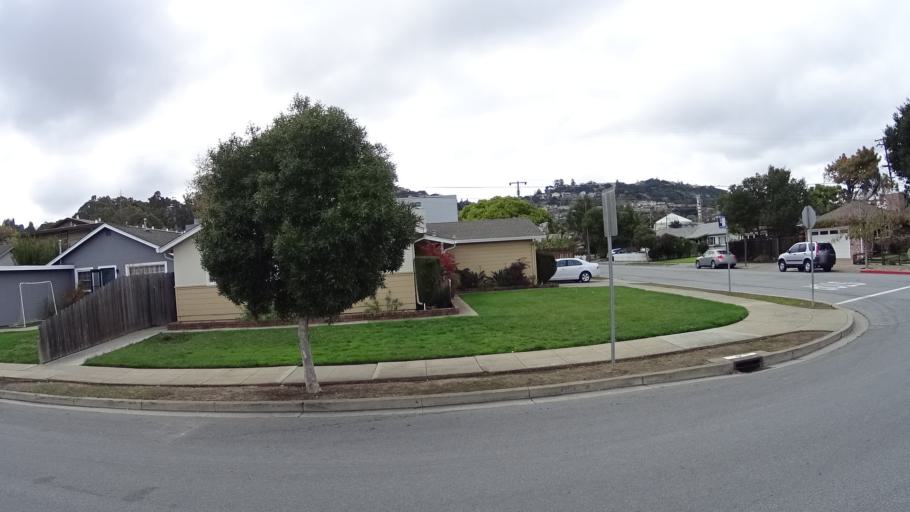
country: US
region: California
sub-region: San Mateo County
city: Belmont
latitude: 37.5299
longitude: -122.2846
